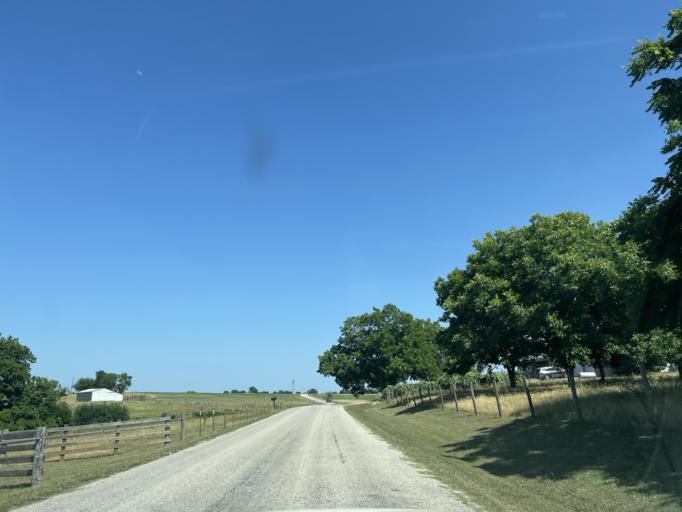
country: US
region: Texas
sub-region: Washington County
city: Brenham
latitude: 30.1703
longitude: -96.3350
